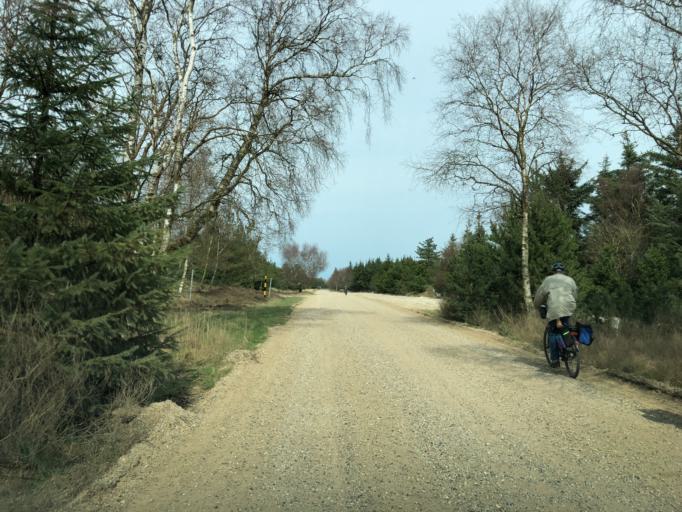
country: DK
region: South Denmark
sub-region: Varde Kommune
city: Oksbol
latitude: 55.6135
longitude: 8.1659
